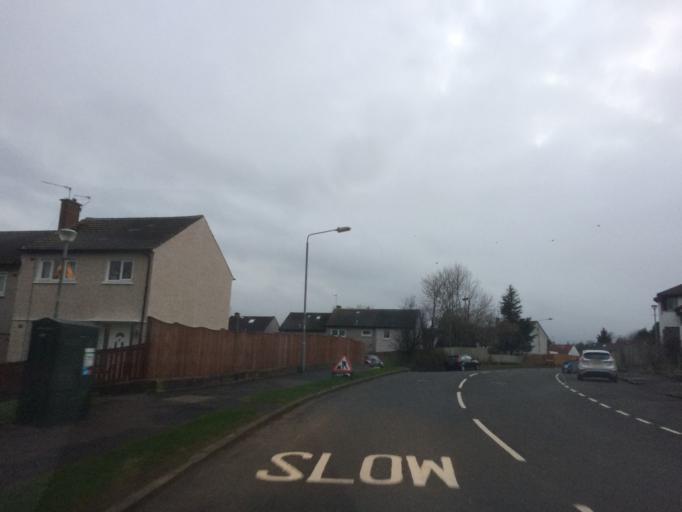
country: GB
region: Scotland
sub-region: East Renfrewshire
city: Newton Mearns
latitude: 55.7828
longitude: -4.3345
